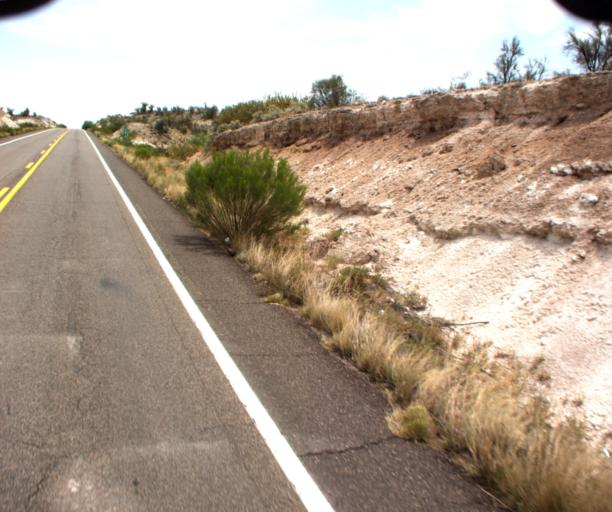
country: US
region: Arizona
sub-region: Graham County
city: Bylas
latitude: 33.2393
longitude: -110.2551
